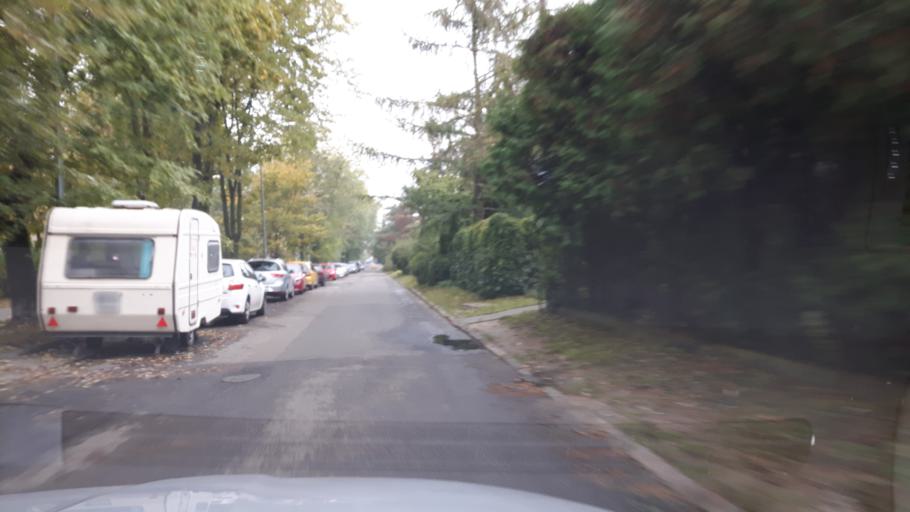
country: PL
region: Masovian Voivodeship
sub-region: Warszawa
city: Praga Poludnie
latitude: 52.2510
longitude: 21.0969
